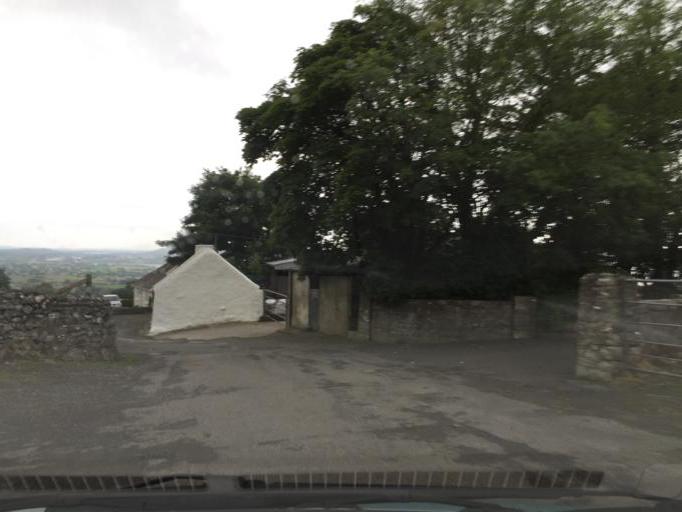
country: IE
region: Connaught
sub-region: Sligo
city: Strandhill
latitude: 54.2531
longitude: -8.5579
